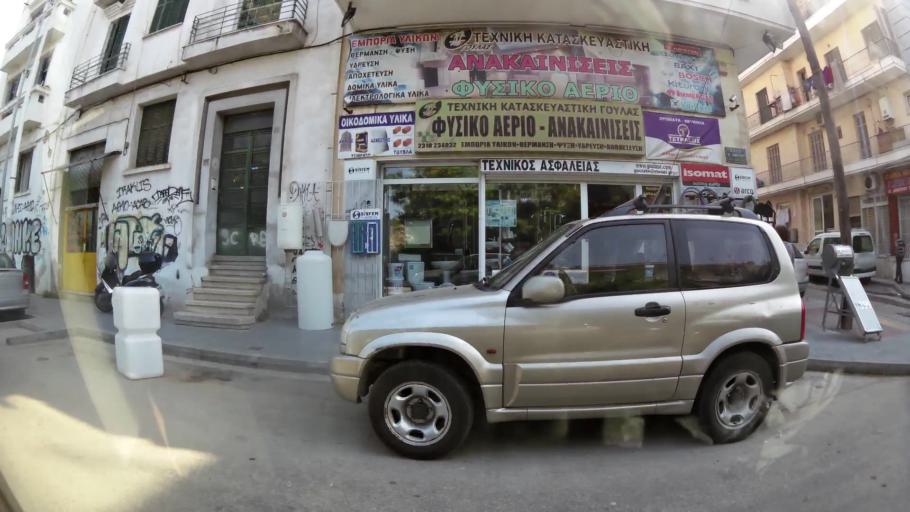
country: GR
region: Central Macedonia
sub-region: Nomos Thessalonikis
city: Thessaloniki
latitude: 40.6436
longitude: 22.9374
